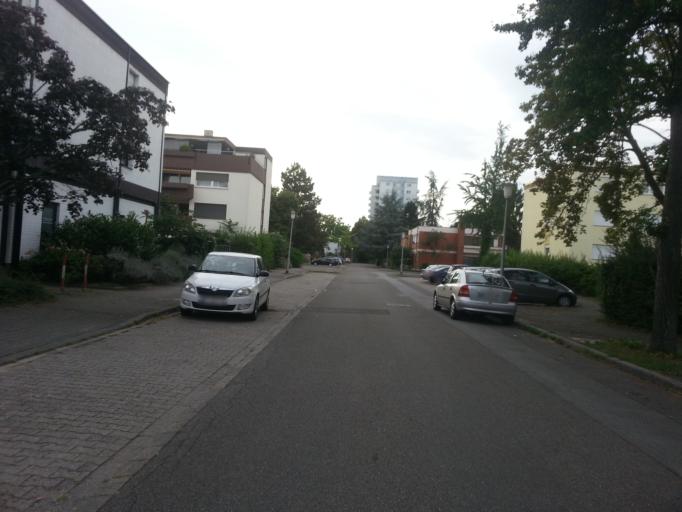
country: DE
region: Rheinland-Pfalz
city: Altrip
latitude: 49.4591
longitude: 8.4738
